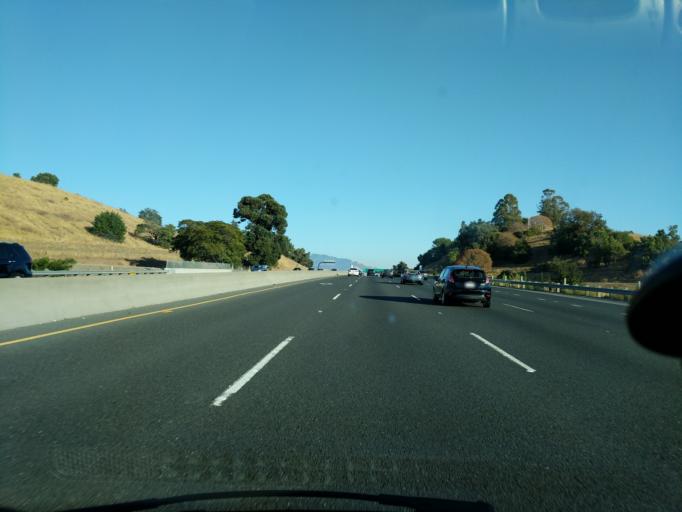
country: US
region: California
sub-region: Contra Costa County
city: Vine Hill
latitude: 38.0023
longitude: -122.0792
